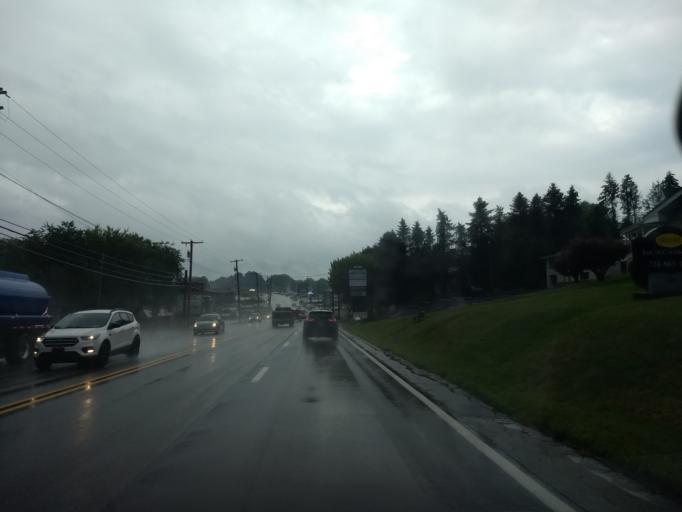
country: US
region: Pennsylvania
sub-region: Westmoreland County
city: Irwin
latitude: 40.3357
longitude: -79.7450
